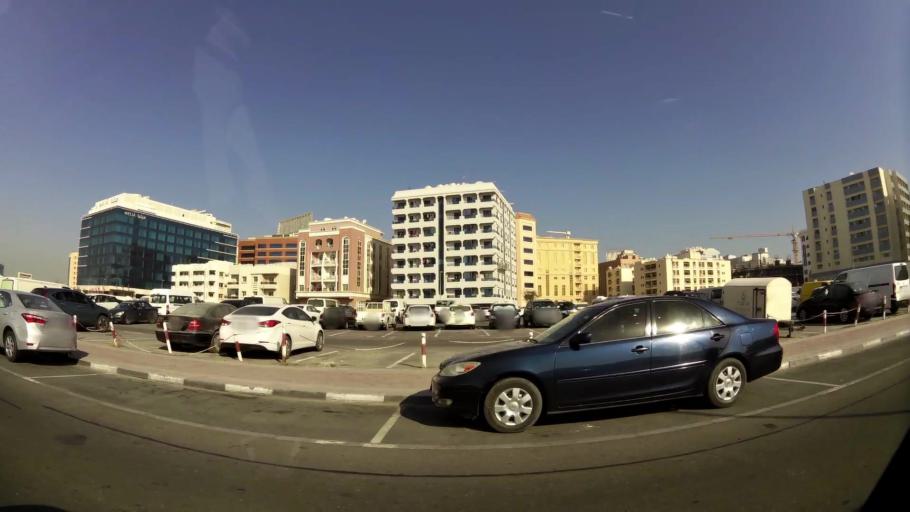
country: AE
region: Ash Shariqah
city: Sharjah
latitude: 25.2558
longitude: 55.2871
